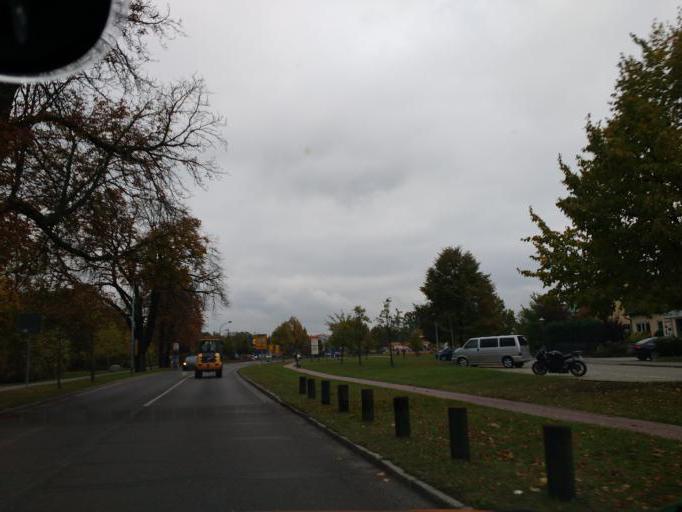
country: DE
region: Brandenburg
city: Ludwigsfelde
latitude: 52.2986
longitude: 13.2641
